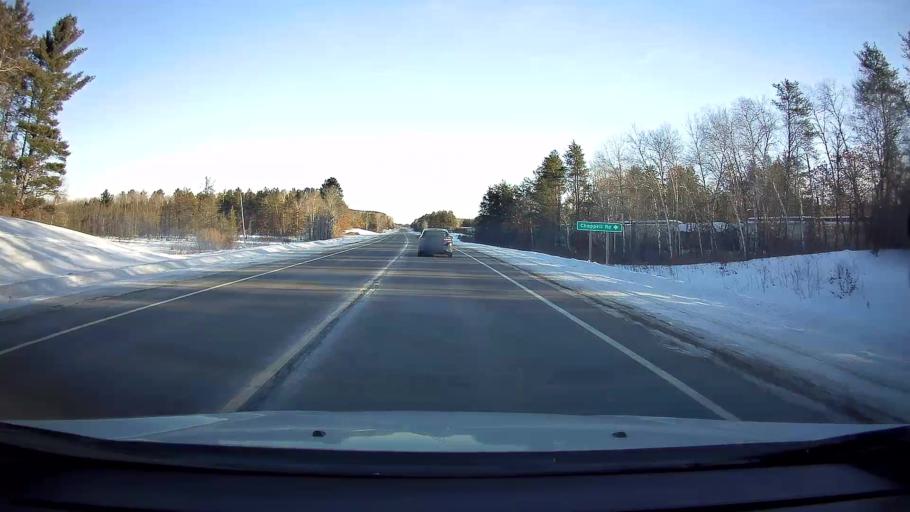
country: US
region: Wisconsin
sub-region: Washburn County
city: Spooner
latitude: 45.9234
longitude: -91.7264
